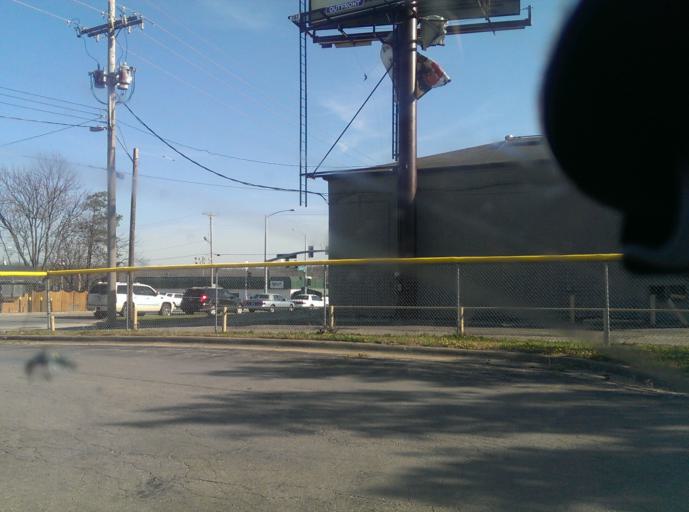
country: US
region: Missouri
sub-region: Jackson County
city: Grandview
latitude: 38.8831
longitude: -94.5868
